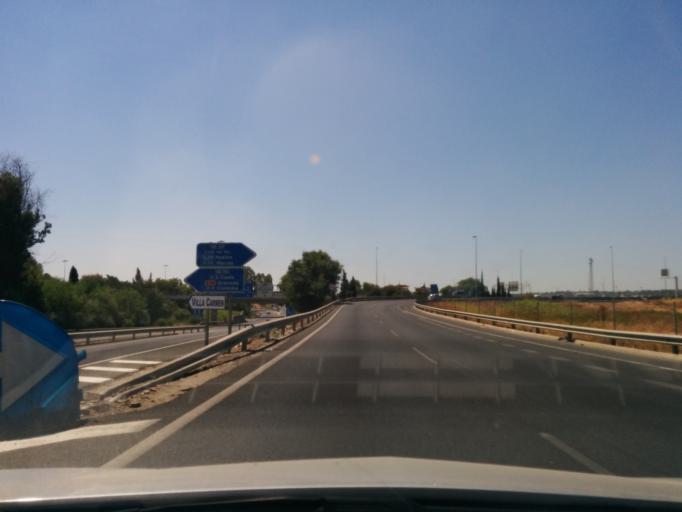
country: ES
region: Andalusia
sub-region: Provincia de Sevilla
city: San Juan de Aznalfarache
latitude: 37.3742
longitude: -6.0158
